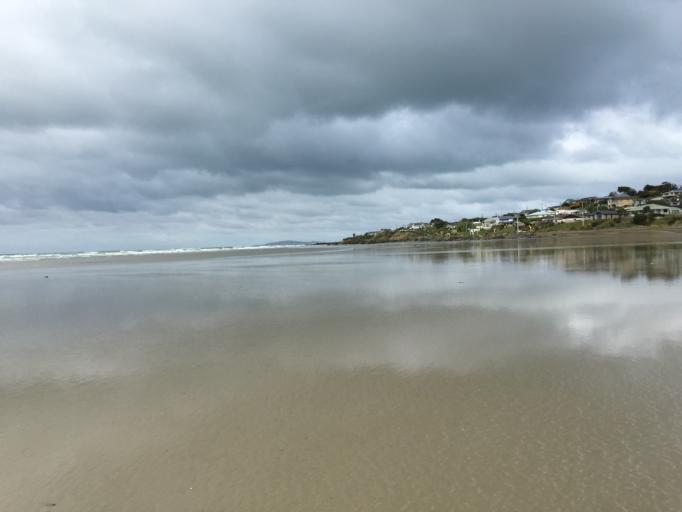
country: NZ
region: Southland
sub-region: Southland District
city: Riverton
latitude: -46.3664
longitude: 168.0227
